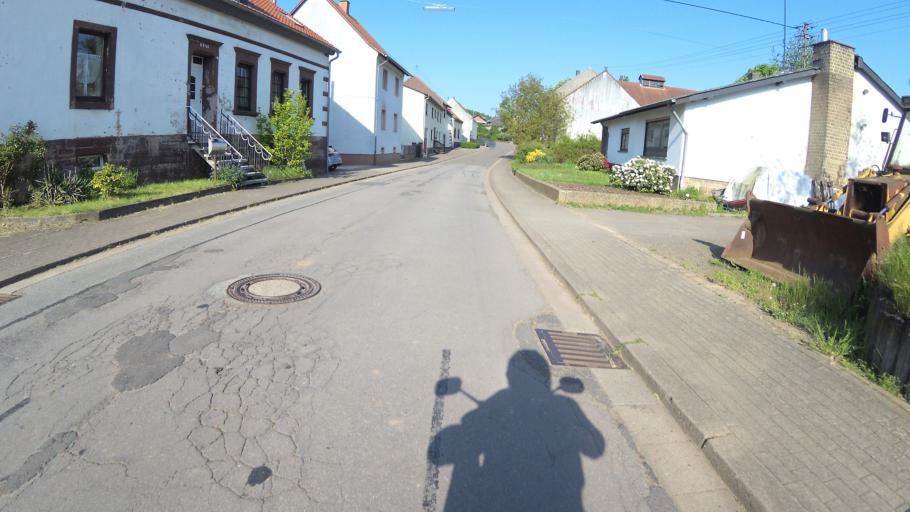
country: DE
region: Saarland
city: Illingen
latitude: 49.3984
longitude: 7.0294
